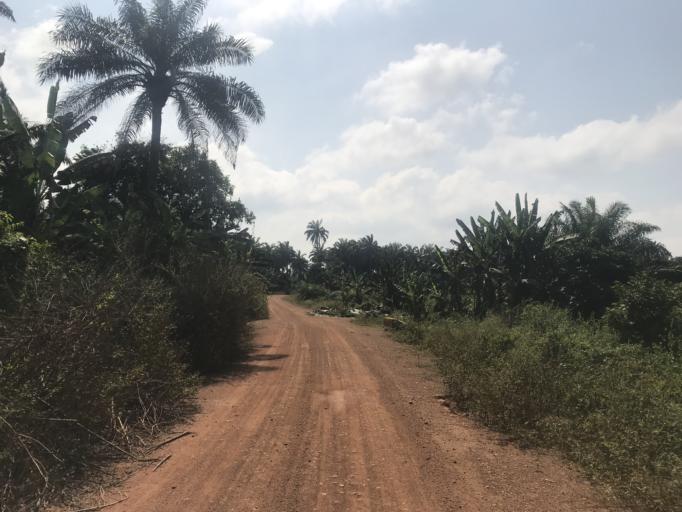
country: NG
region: Osun
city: Ibokun
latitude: 7.8196
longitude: 4.6442
